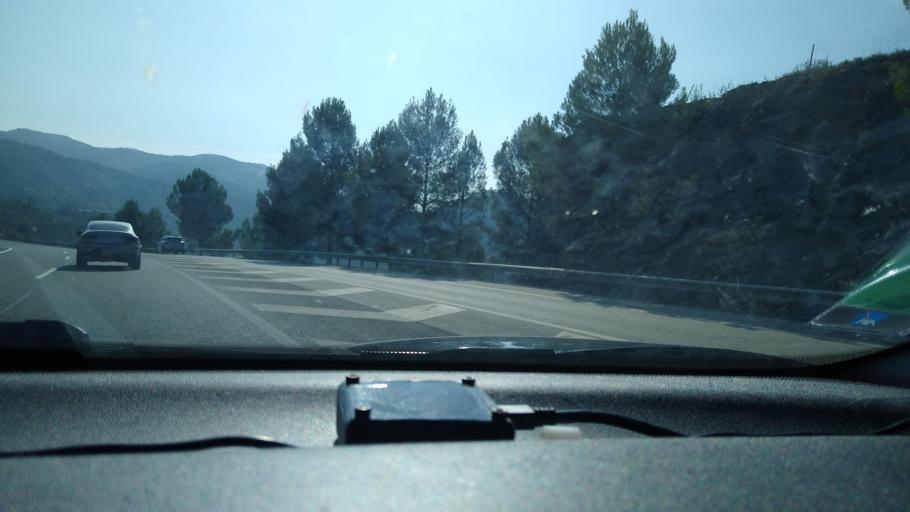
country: ES
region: Catalonia
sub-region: Provincia de Barcelona
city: Monistrol de Montserrat
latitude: 41.6457
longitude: 1.8630
